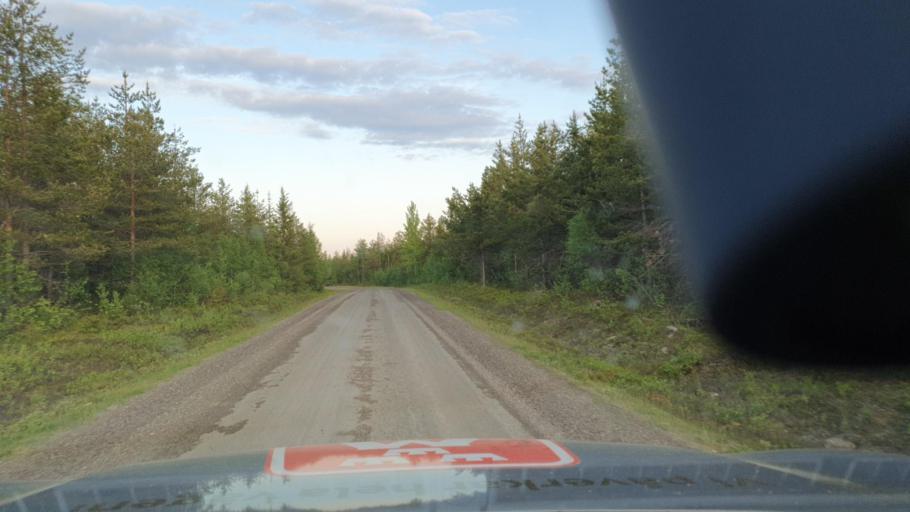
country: SE
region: Norrbotten
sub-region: Bodens Kommun
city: Boden
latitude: 66.4965
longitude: 21.5599
